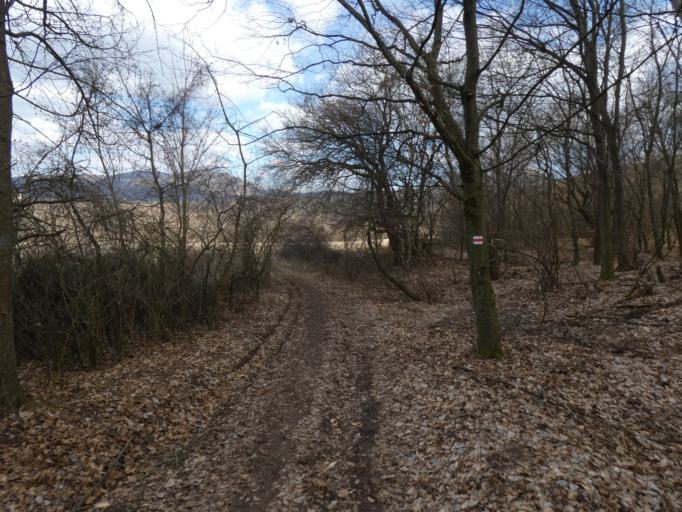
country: HU
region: Pest
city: Szob
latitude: 47.9278
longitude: 18.8157
